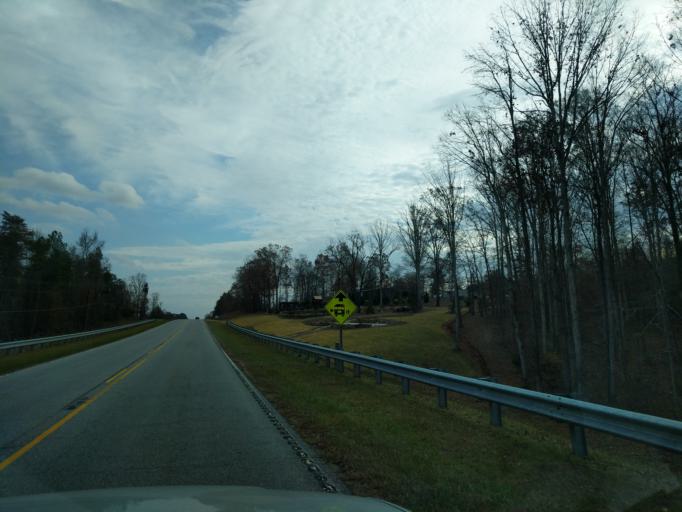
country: US
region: Georgia
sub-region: Franklin County
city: Gumlog
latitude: 34.5208
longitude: -83.0490
